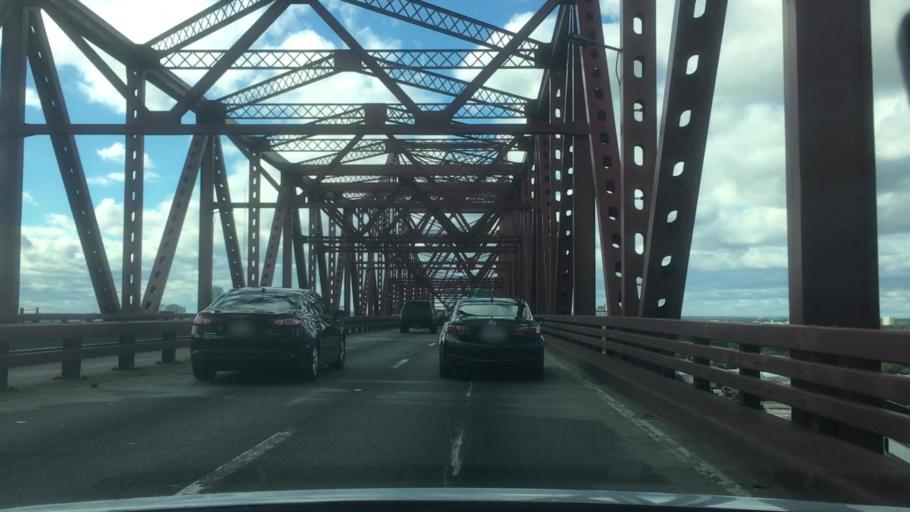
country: US
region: Florida
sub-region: Duval County
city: Jacksonville
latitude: 30.3274
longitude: -81.6241
